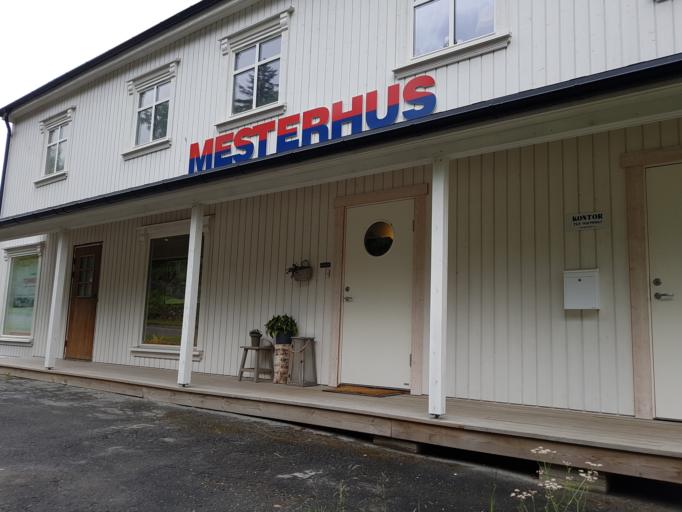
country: NO
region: Sor-Trondelag
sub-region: Selbu
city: Mebonden
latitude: 63.2305
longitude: 11.0341
